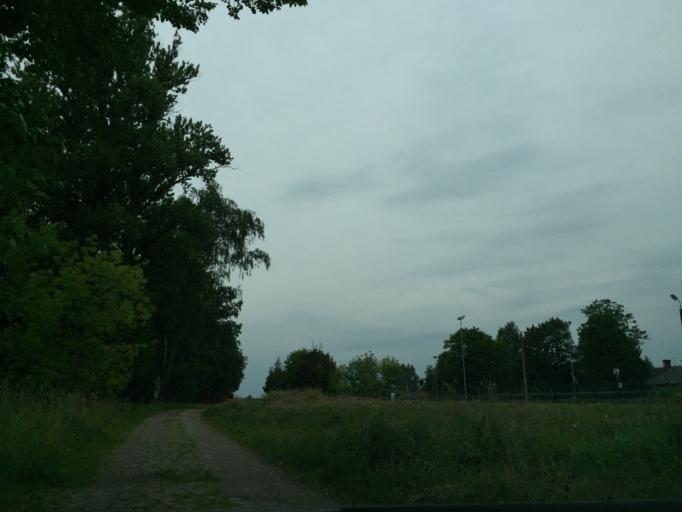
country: LV
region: Zilupes
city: Zilupe
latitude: 56.3916
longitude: 28.1123
